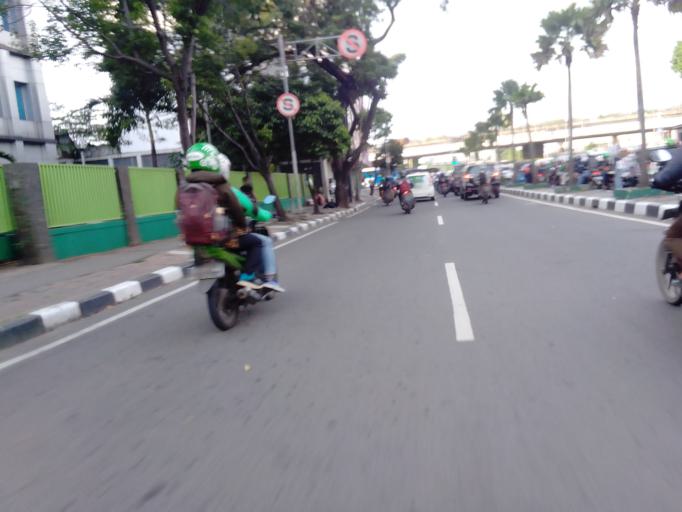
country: ID
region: Jakarta Raya
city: Jakarta
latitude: -6.1791
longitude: 106.8412
